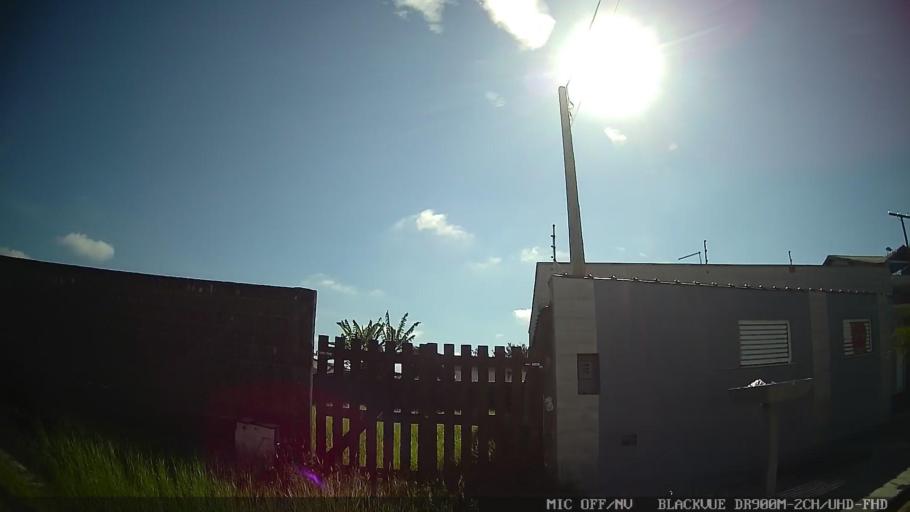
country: BR
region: Sao Paulo
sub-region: Peruibe
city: Peruibe
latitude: -24.2745
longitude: -46.9471
